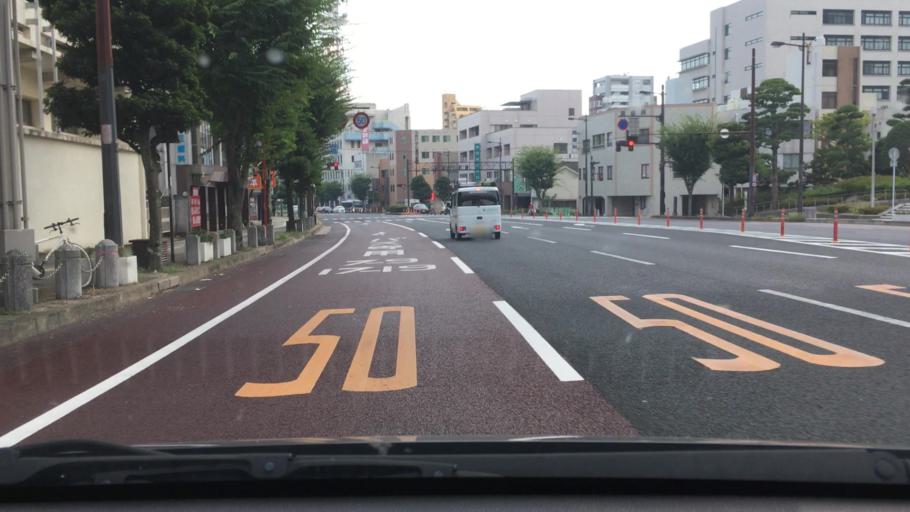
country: JP
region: Nagasaki
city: Sasebo
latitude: 33.1801
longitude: 129.7159
